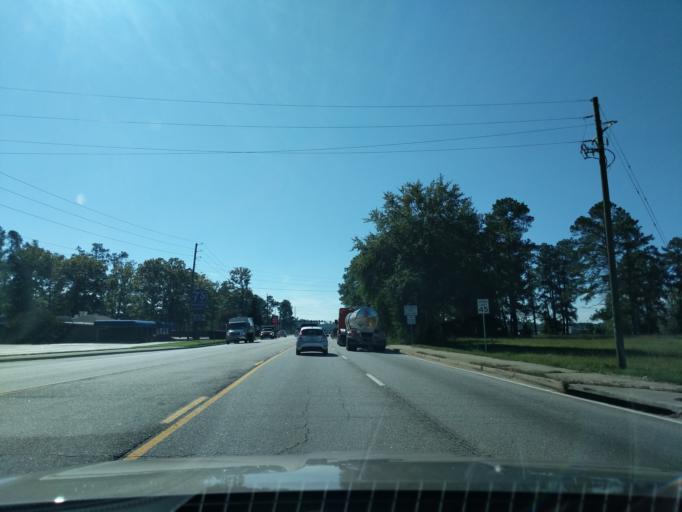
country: US
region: Georgia
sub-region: Richmond County
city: Augusta
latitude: 33.3970
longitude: -82.0055
